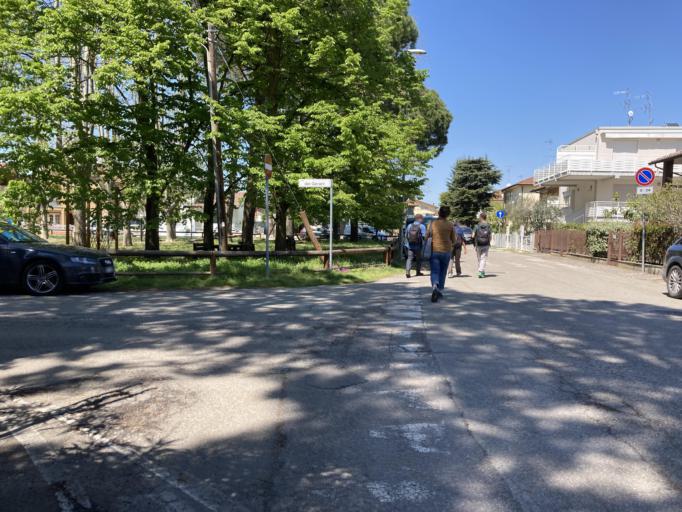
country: IT
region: Emilia-Romagna
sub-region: Provincia di Ravenna
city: Cervia
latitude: 44.2619
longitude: 12.3409
